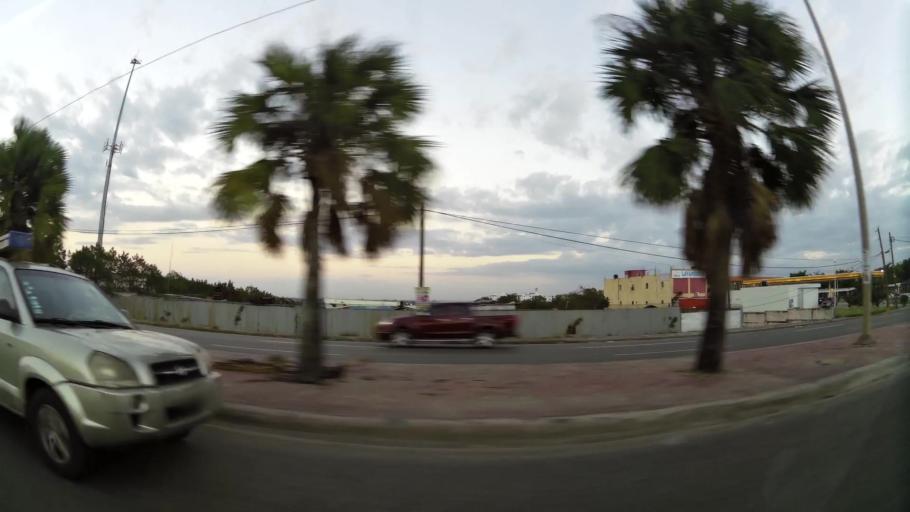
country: DO
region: Nacional
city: La Agustina
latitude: 18.5551
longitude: -69.9439
